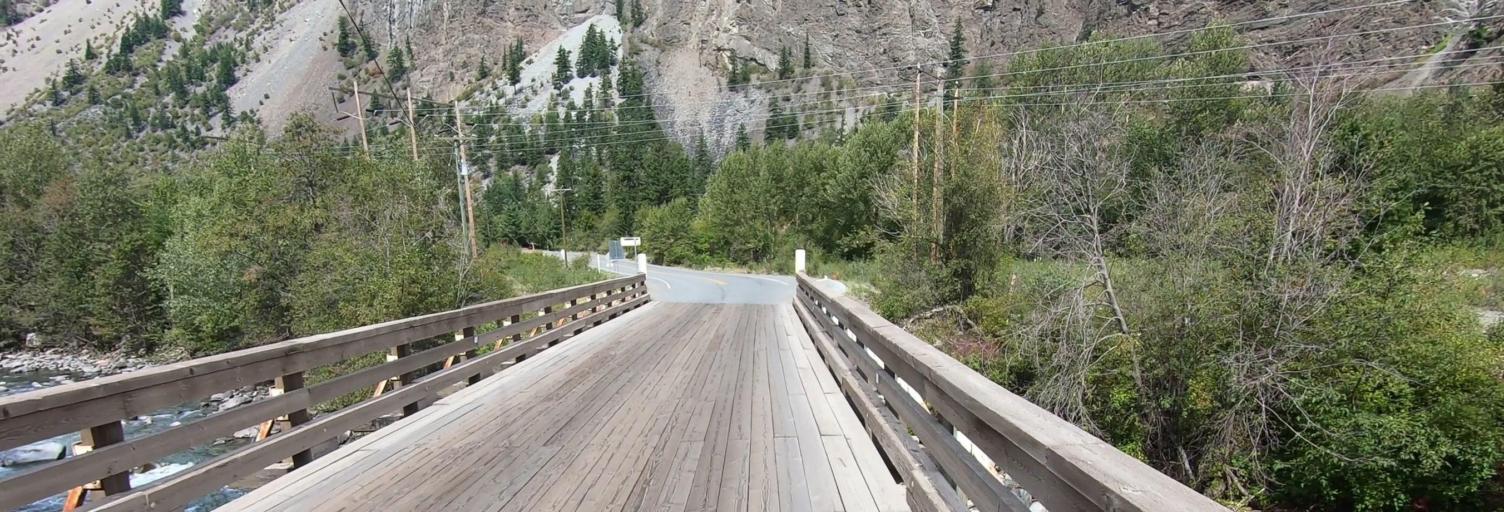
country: CA
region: British Columbia
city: Lillooet
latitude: 50.6691
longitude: -121.9653
